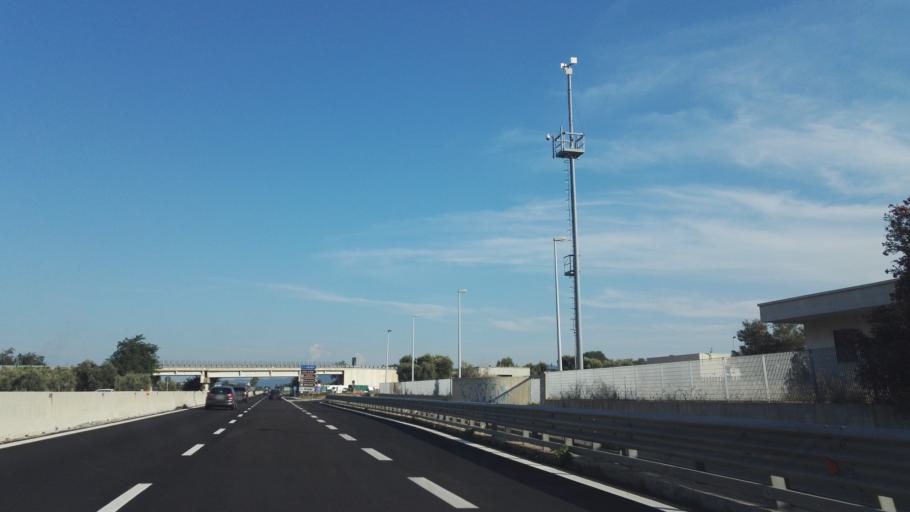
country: IT
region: Apulia
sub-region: Provincia di Brindisi
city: Fasano
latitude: 40.8525
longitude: 17.3559
